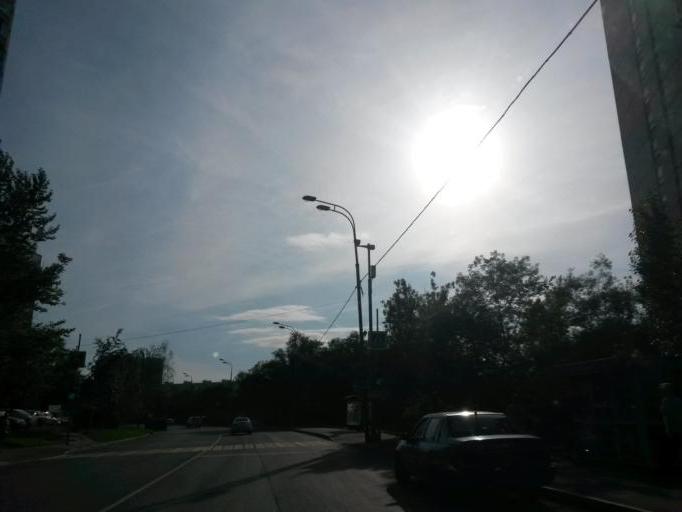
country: RU
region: Moscow
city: Orekhovo-Borisovo
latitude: 55.6266
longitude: 37.7361
